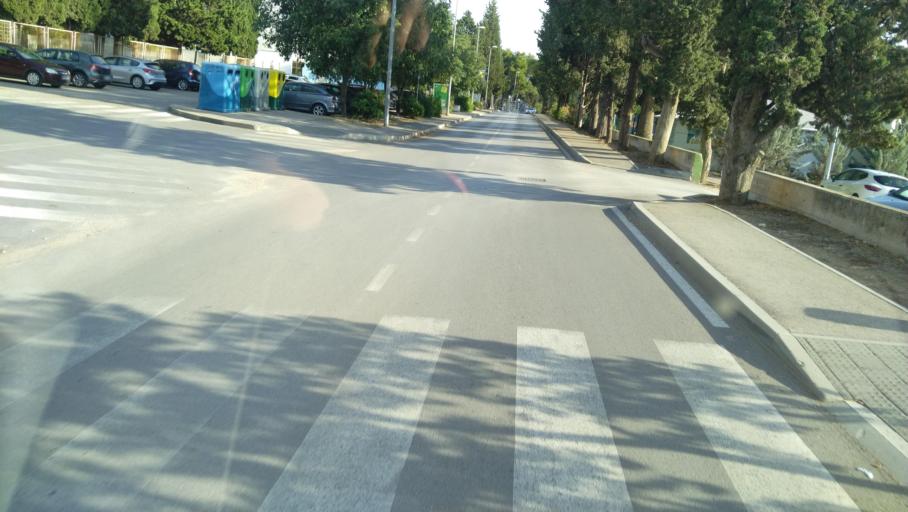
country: HR
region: Sibensko-Kniniska
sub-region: Grad Sibenik
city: Sibenik
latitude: 43.7409
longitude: 15.8990
